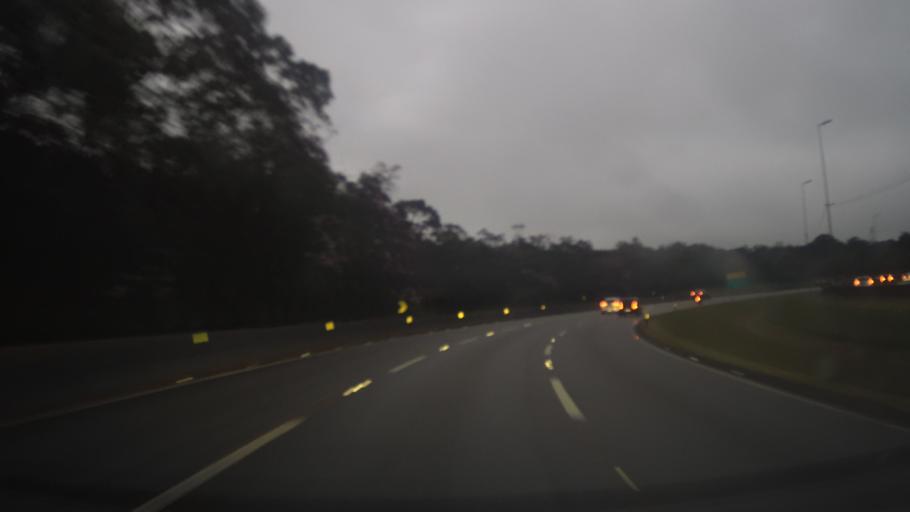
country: BR
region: Sao Paulo
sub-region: Cubatao
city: Cubatao
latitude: -23.8953
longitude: -46.5667
